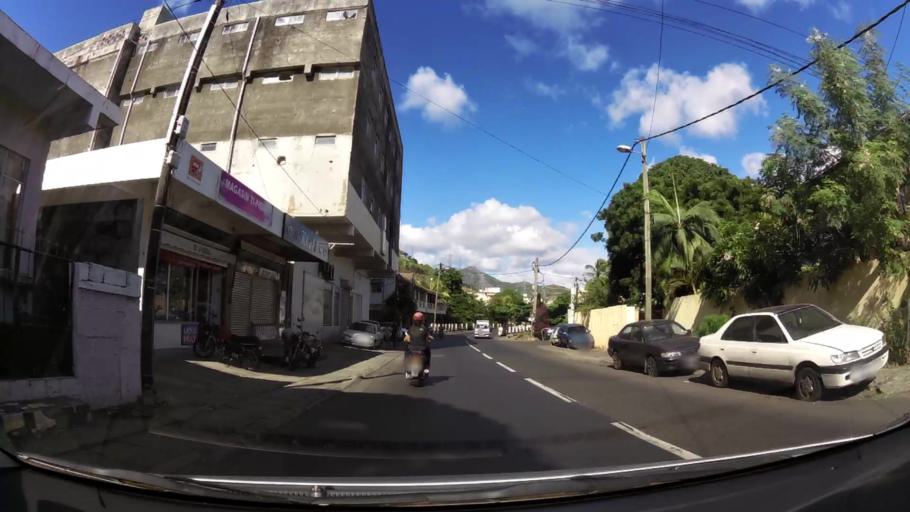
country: MU
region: Pamplemousses
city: Le Hochet
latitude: -20.1506
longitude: 57.5225
